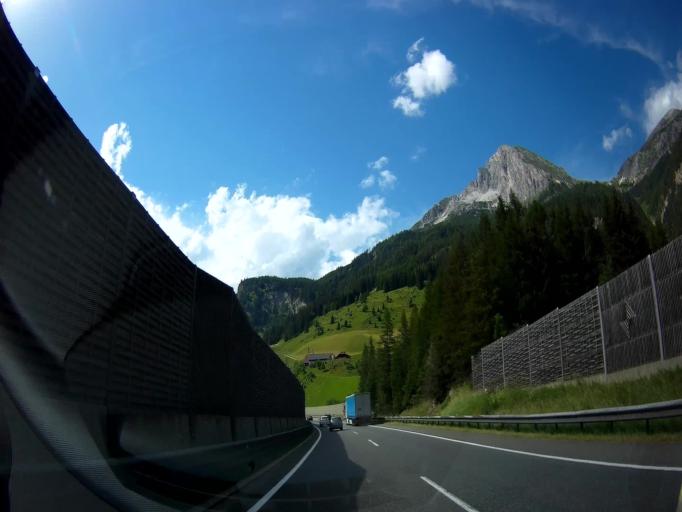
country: AT
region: Salzburg
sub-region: Politischer Bezirk Tamsweg
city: Zederhaus
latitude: 47.1672
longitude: 13.4655
